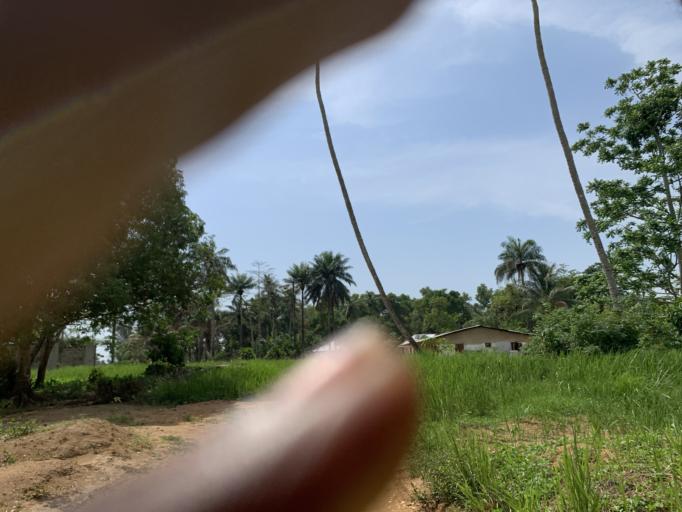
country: SL
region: Western Area
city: Waterloo
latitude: 8.3628
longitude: -13.0471
